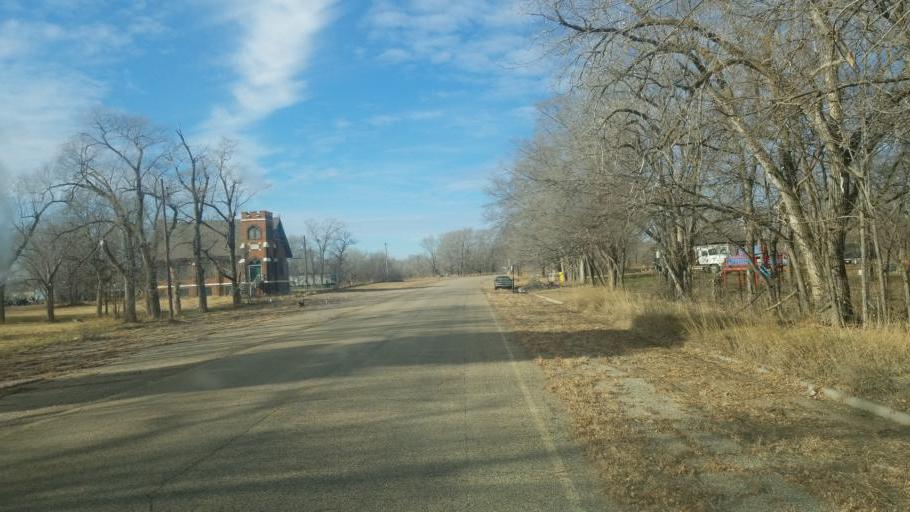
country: US
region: South Dakota
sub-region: Charles Mix County
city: Wagner
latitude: 42.9228
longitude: -98.3876
